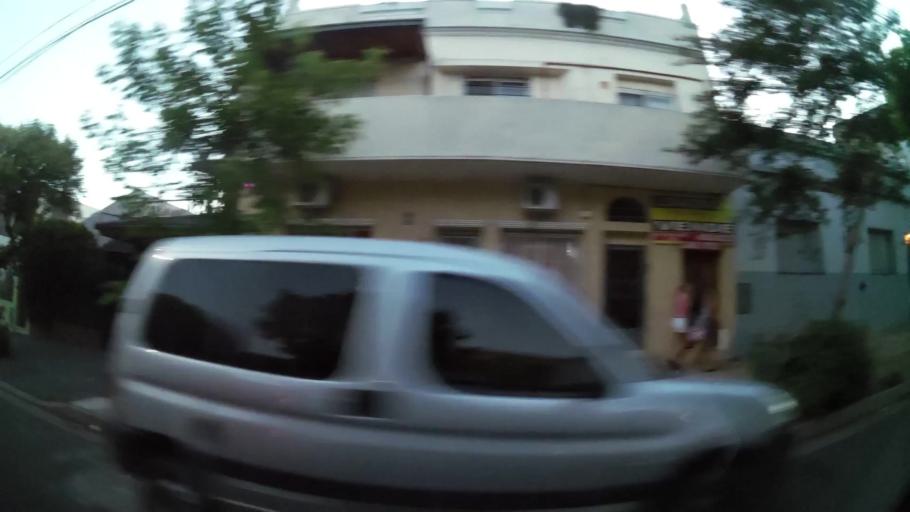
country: AR
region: Buenos Aires F.D.
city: Villa Lugano
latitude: -34.6801
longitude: -58.4747
